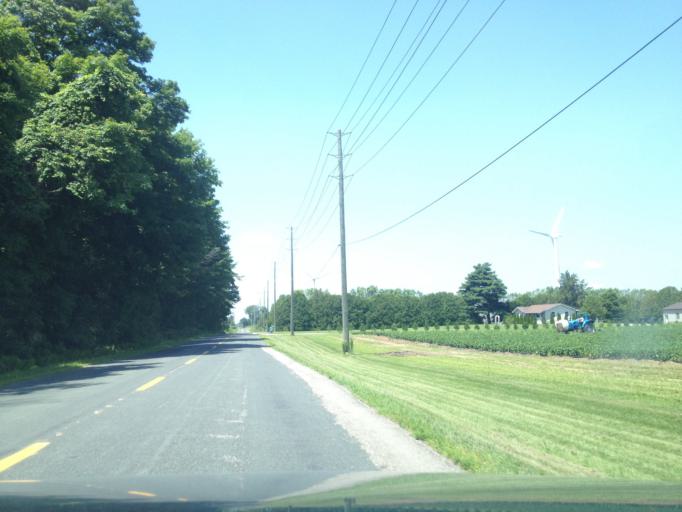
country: CA
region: Ontario
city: Aylmer
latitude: 42.6400
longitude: -80.7277
